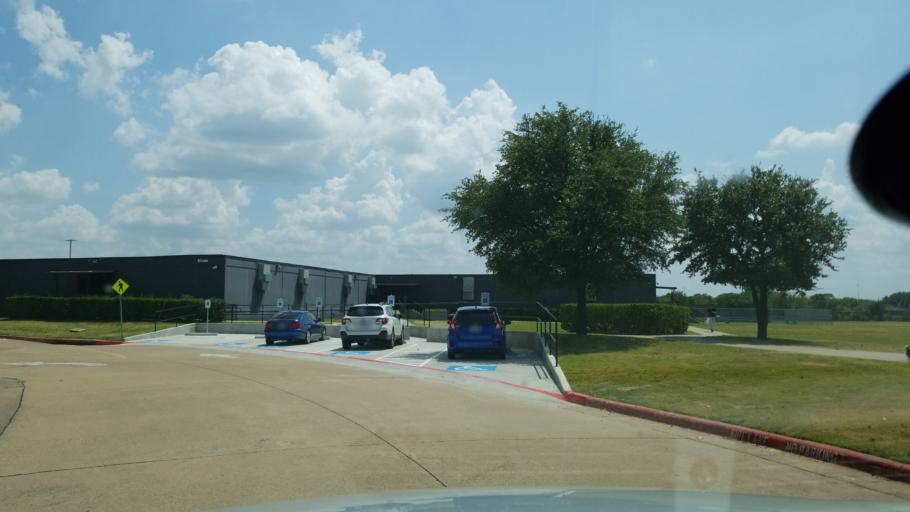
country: US
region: Texas
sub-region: Dallas County
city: Richardson
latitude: 32.9201
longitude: -96.7285
